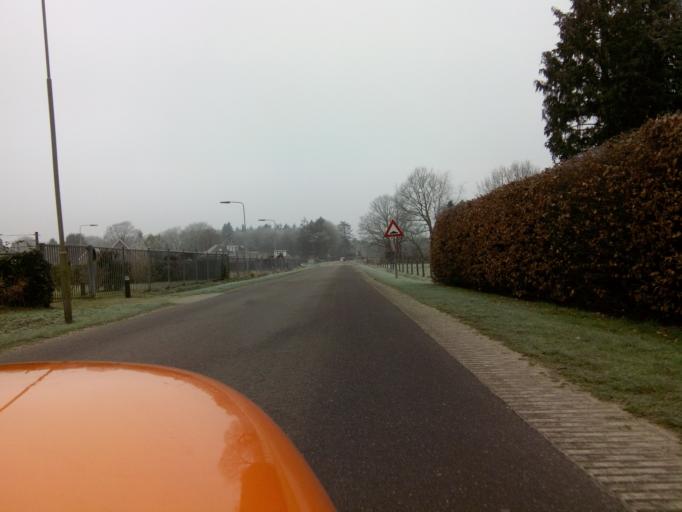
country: NL
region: Gelderland
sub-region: Gemeente Barneveld
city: Voorthuizen
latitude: 52.2197
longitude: 5.6138
